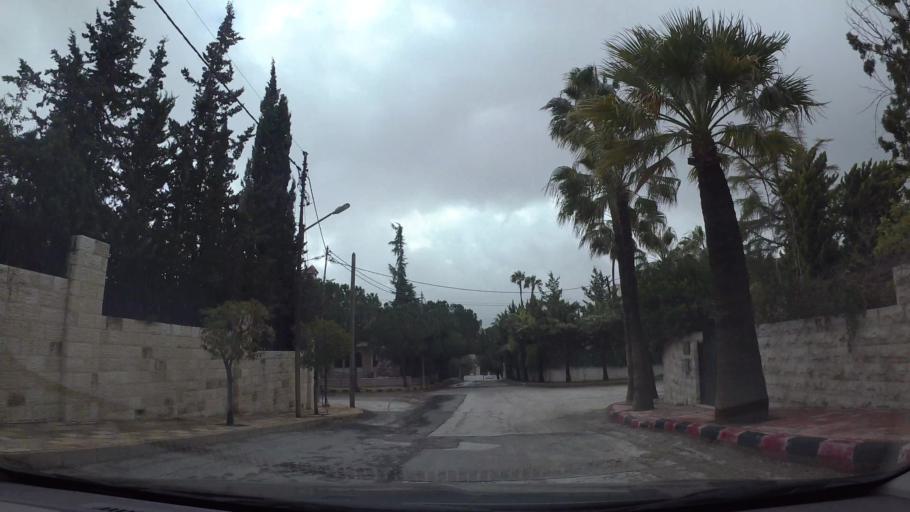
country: JO
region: Amman
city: Amman
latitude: 31.9461
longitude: 35.8935
